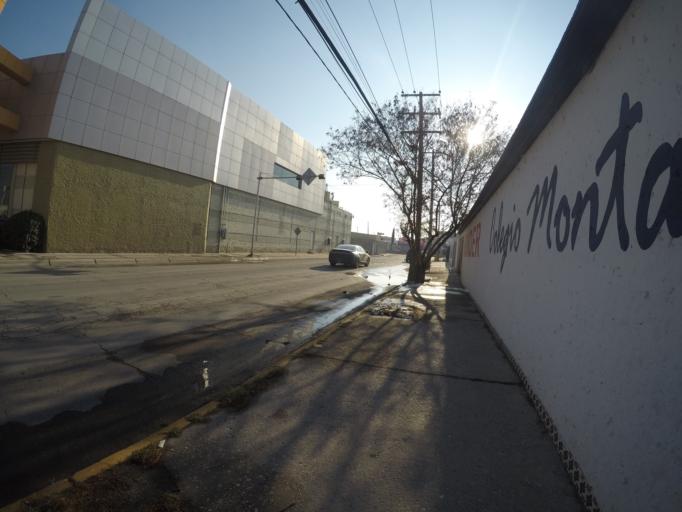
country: MX
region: Chihuahua
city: Ciudad Juarez
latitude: 31.7124
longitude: -106.4113
